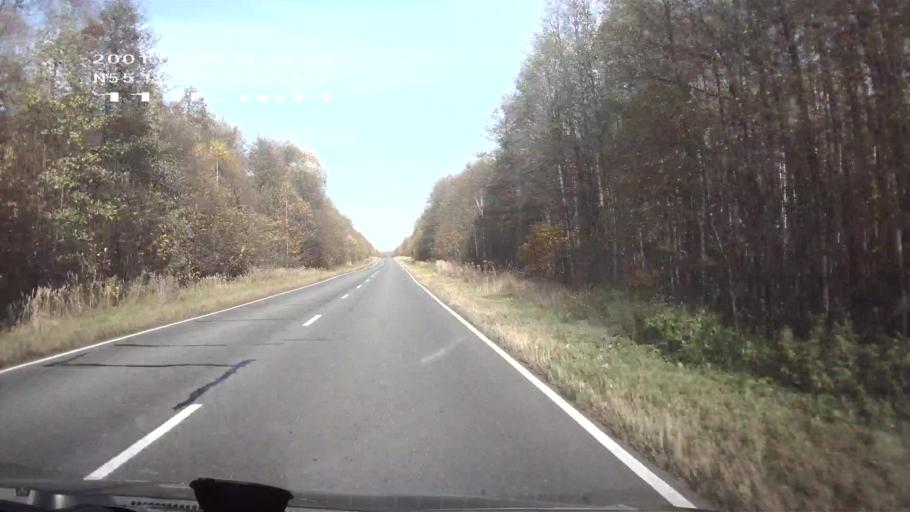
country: RU
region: Chuvashia
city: Buinsk
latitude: 55.1810
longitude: 47.0649
